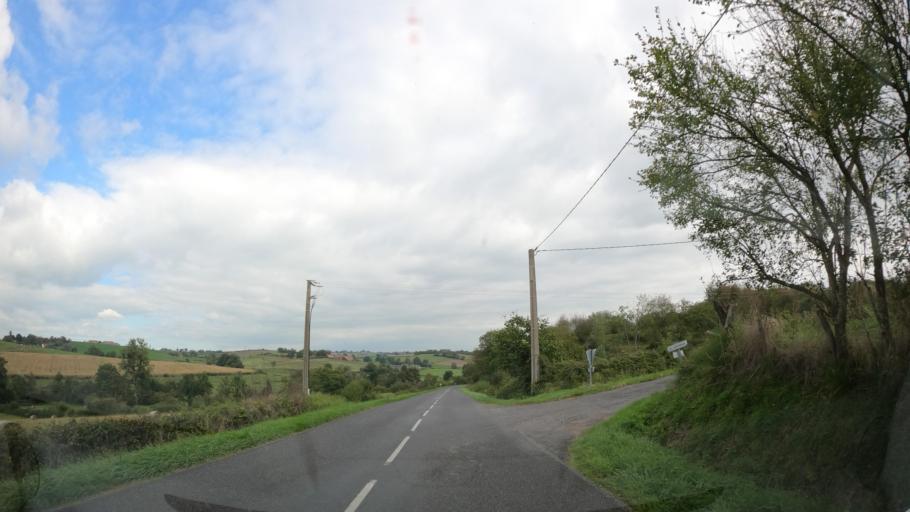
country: FR
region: Auvergne
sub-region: Departement de l'Allier
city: Lapalisse
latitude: 46.3287
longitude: 3.6085
